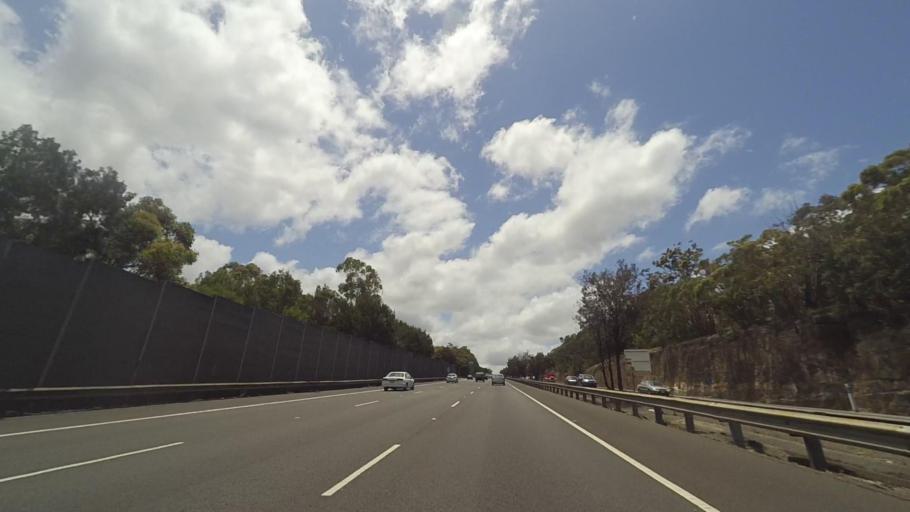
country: AU
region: New South Wales
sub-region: Hornsby Shire
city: Mount Colah
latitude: -33.6871
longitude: 151.1209
